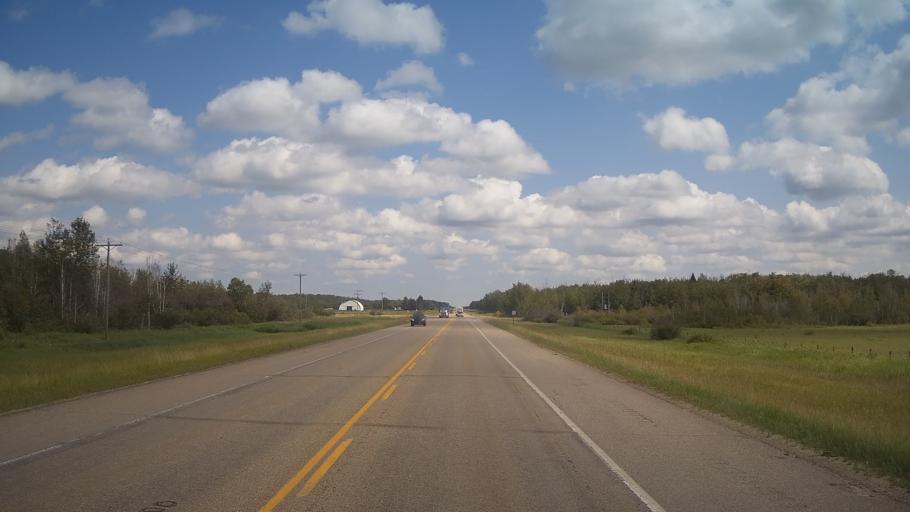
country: CA
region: Alberta
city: Sherwood Park
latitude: 53.3957
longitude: -113.0783
